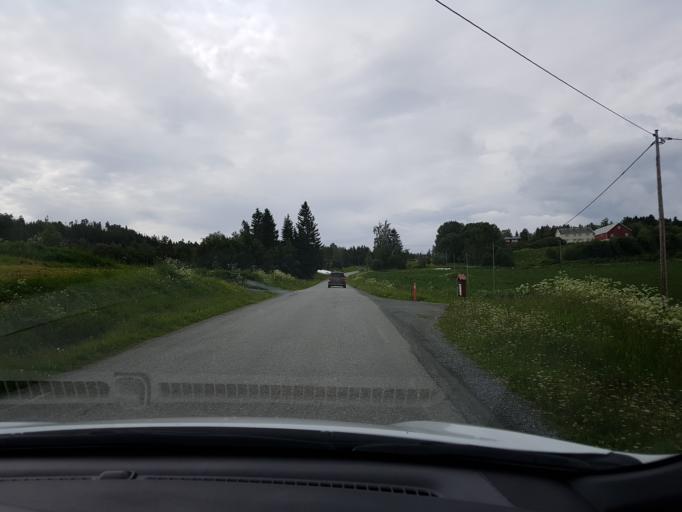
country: NO
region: Nord-Trondelag
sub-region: Frosta
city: Frosta
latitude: 63.6163
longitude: 10.7534
